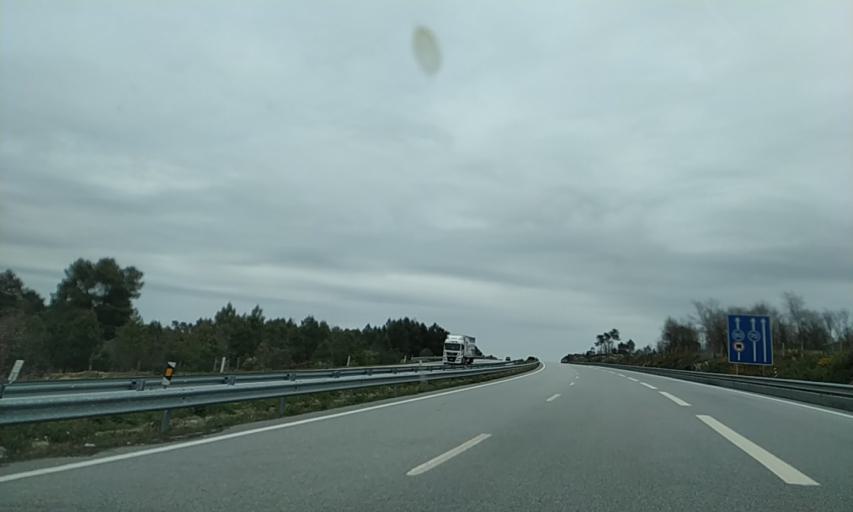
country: PT
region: Viseu
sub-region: Mangualde
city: Mangualde
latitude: 40.6125
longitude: -7.7092
